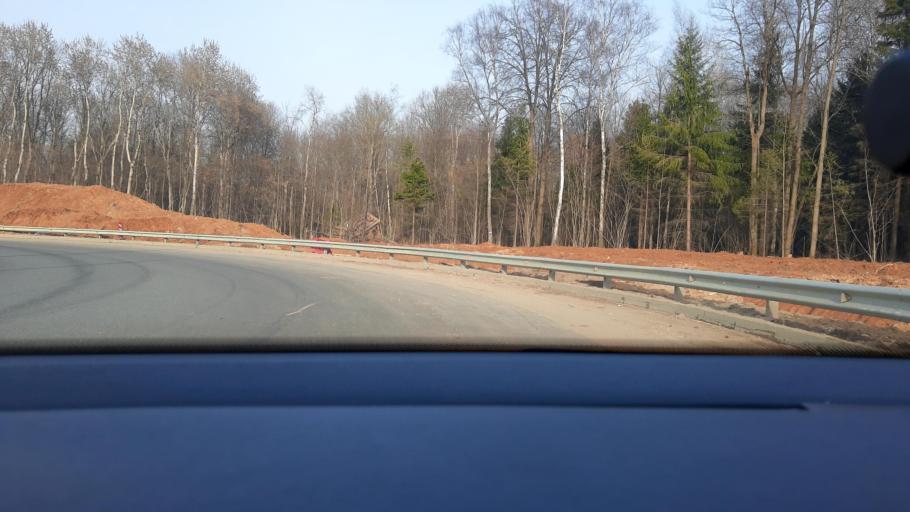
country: RU
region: Moskovskaya
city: Barvikha
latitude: 55.7203
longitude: 37.3165
